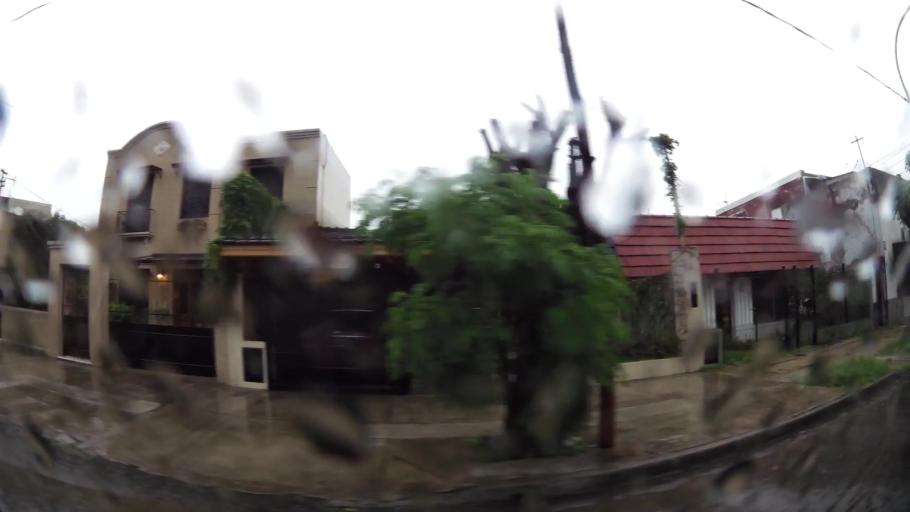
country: AR
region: Buenos Aires
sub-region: Partido de Lanus
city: Lanus
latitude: -34.7090
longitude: -58.4024
